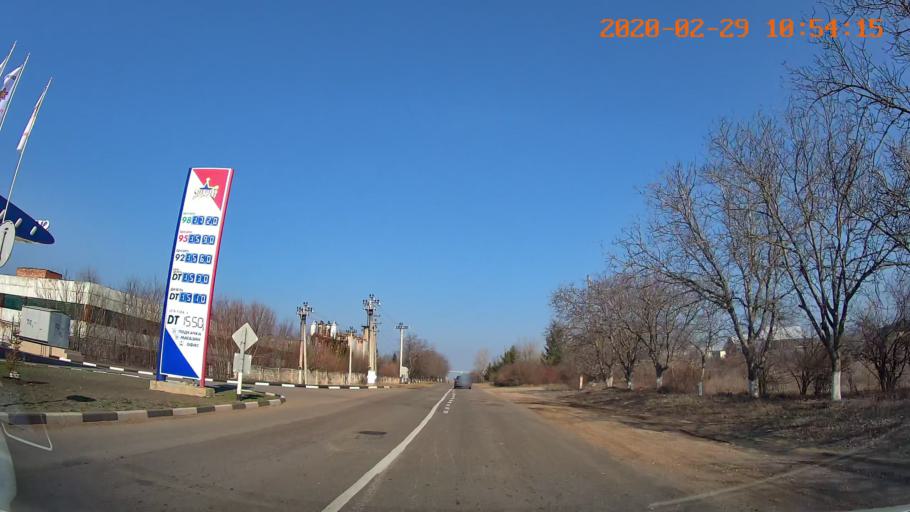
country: MD
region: Telenesti
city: Grigoriopol
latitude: 47.1211
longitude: 29.3278
